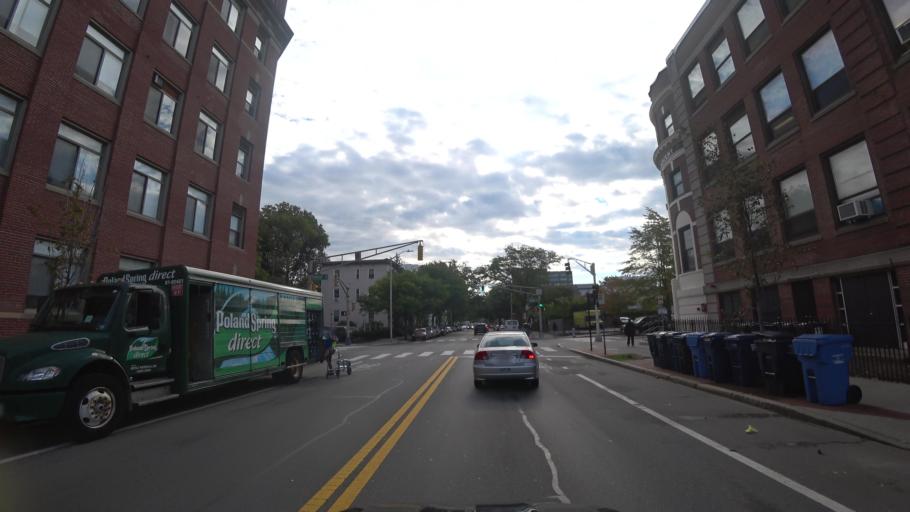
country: US
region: Massachusetts
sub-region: Middlesex County
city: Cambridge
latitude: 42.3673
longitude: -71.0959
